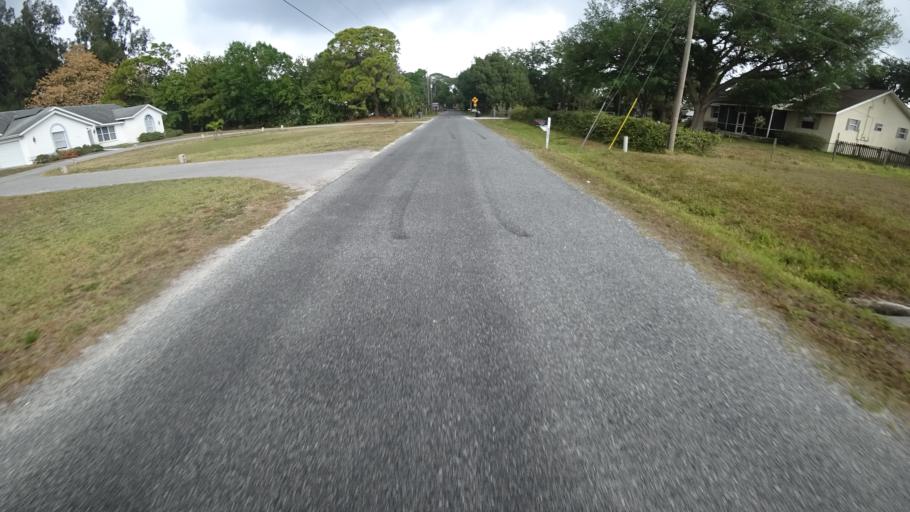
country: US
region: Florida
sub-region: Manatee County
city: Samoset
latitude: 27.4780
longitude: -82.5037
